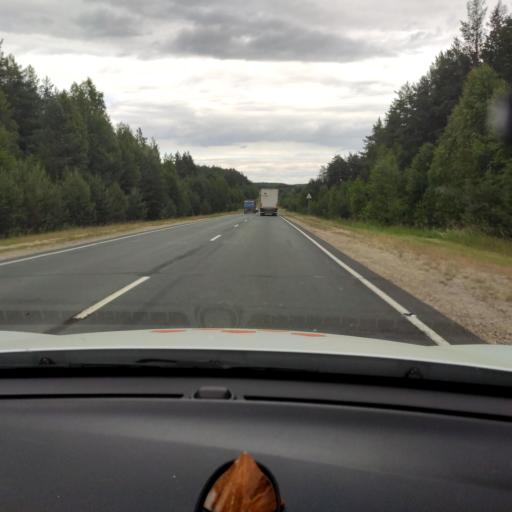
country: RU
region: Mariy-El
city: Volzhsk
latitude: 55.9024
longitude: 48.3831
